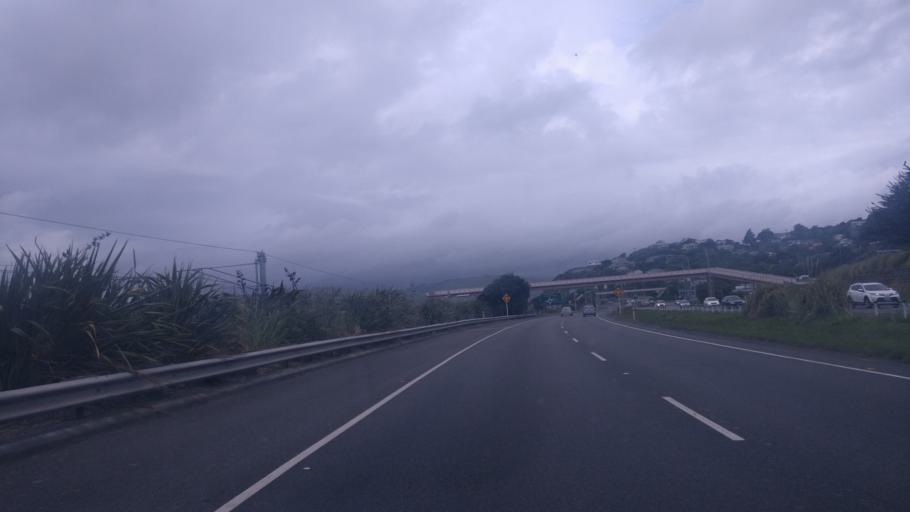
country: NZ
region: Wellington
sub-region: Porirua City
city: Porirua
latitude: -41.1084
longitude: 174.8634
